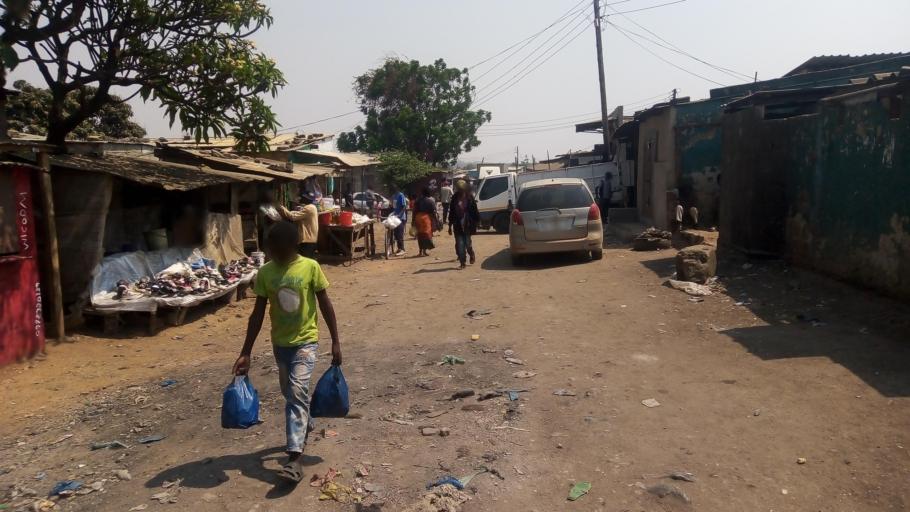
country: ZM
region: Lusaka
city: Lusaka
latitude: -15.4471
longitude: 28.3782
